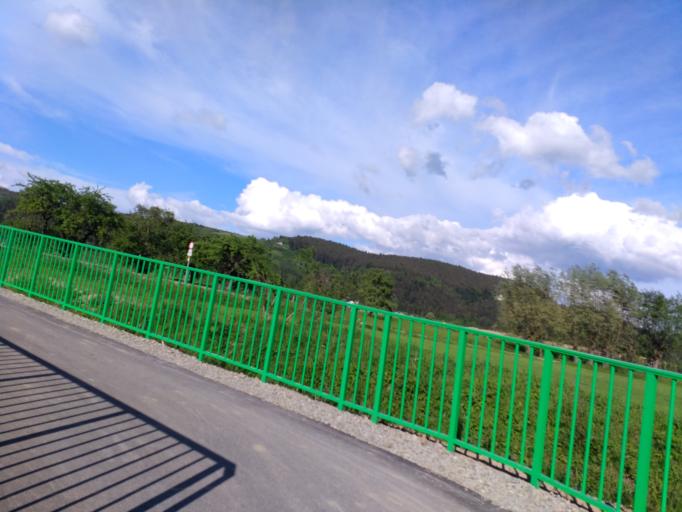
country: PL
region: Lesser Poland Voivodeship
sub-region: Powiat nowosadecki
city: Lacko
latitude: 49.5452
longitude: 20.4613
